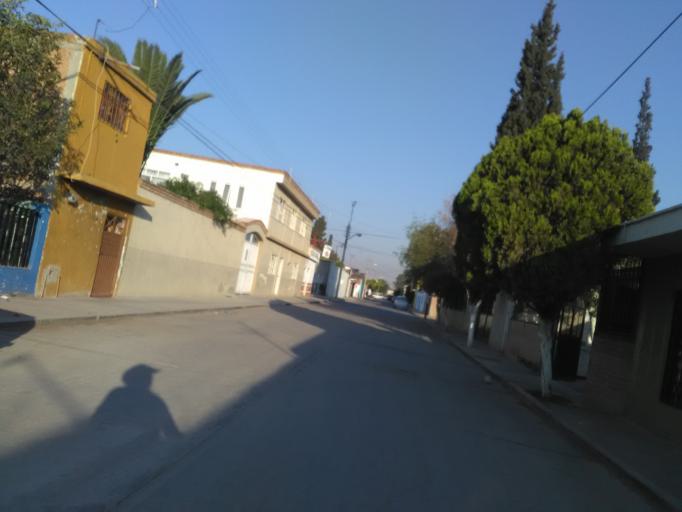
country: MX
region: Durango
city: Victoria de Durango
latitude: 24.0388
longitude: -104.6441
